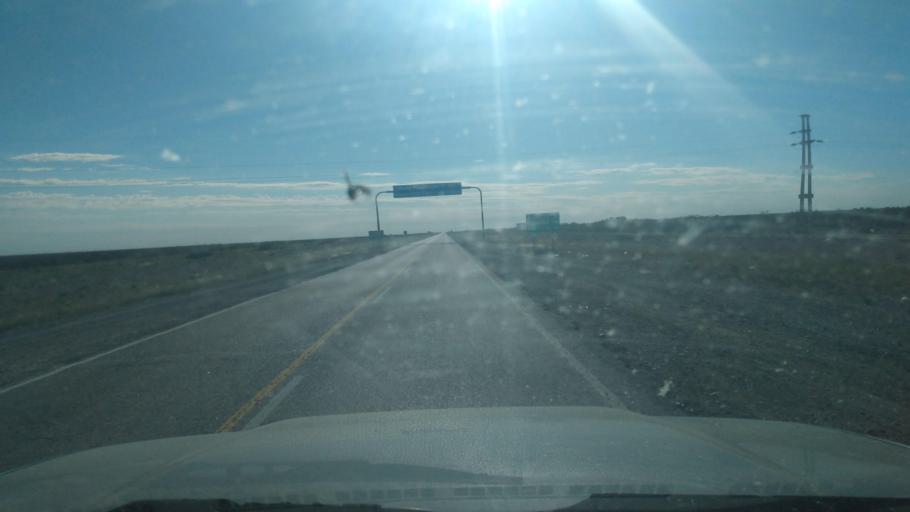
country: AR
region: La Pampa
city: Veinticinco de Mayo
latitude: -37.6603
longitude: -67.7449
